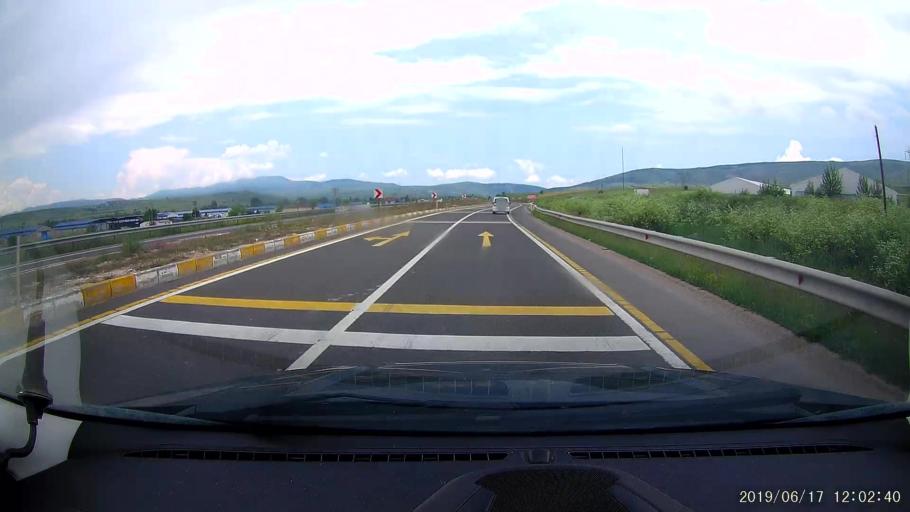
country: TR
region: Cankiri
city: Cerkes
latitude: 40.8242
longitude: 32.8408
